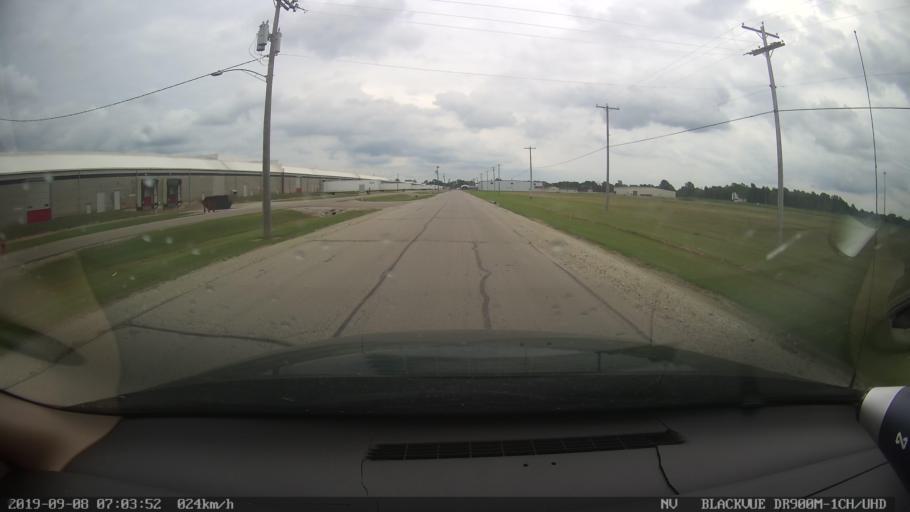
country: US
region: Ohio
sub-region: Richland County
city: Shelby
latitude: 40.8970
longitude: -82.6751
